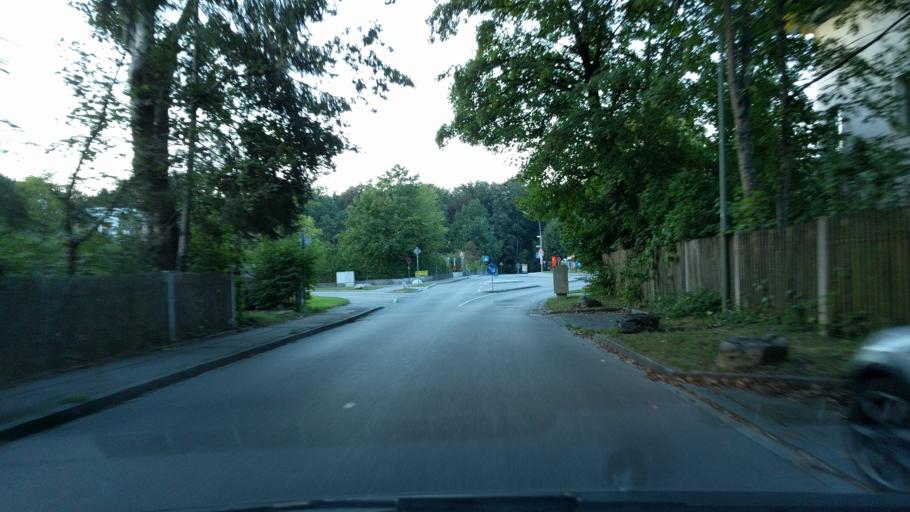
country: DE
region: Bavaria
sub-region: Upper Bavaria
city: Pullach im Isartal
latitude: 48.0667
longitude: 11.5479
